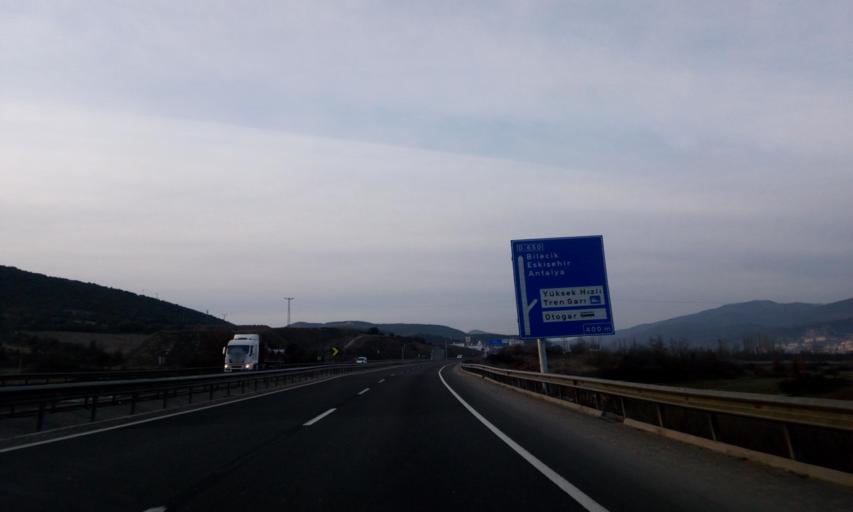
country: TR
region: Bilecik
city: Bilecik
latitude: 40.1407
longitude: 30.0259
